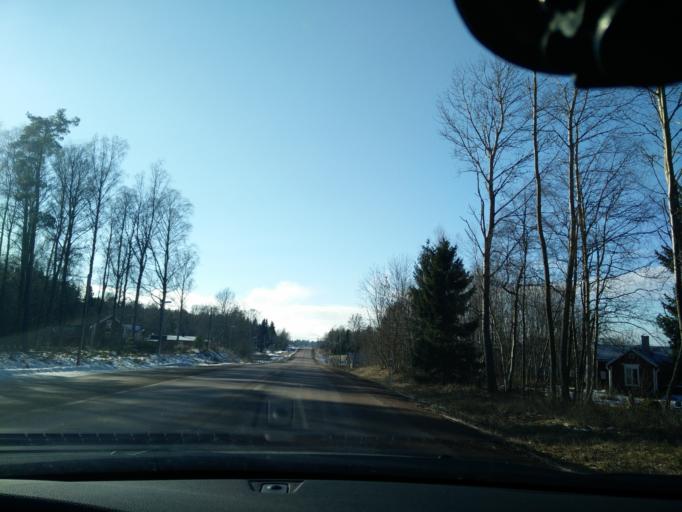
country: AX
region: Alands landsbygd
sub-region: Eckeroe
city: Eckeroe
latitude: 60.2145
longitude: 19.6356
